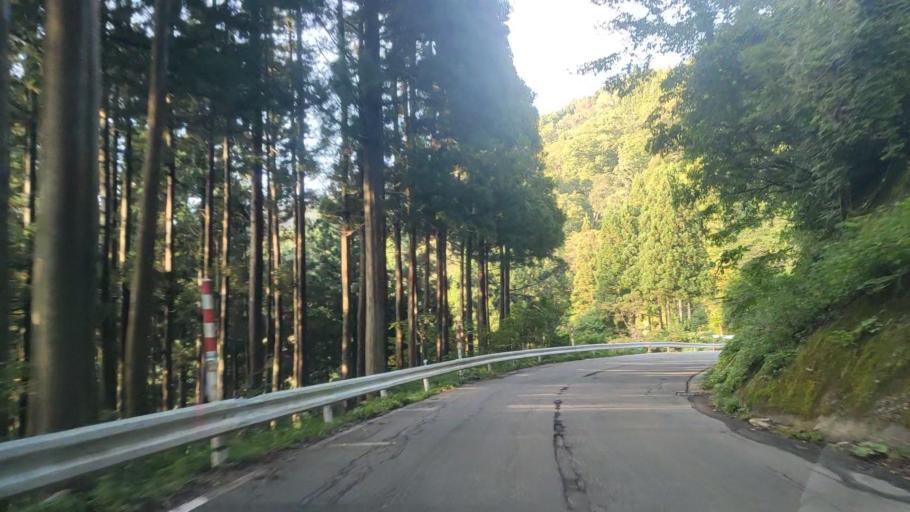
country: JP
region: Toyama
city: Yatsuomachi-higashikumisaka
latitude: 36.4805
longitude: 137.0307
